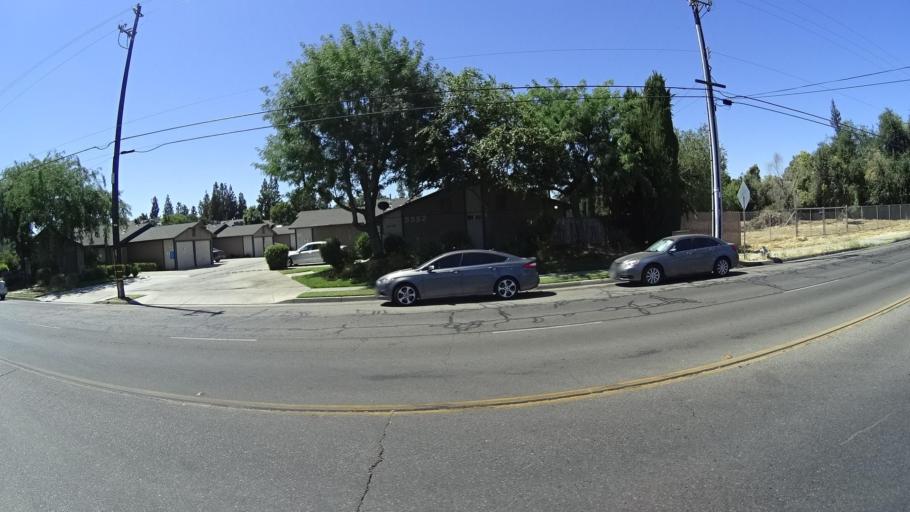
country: US
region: California
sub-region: Fresno County
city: Sunnyside
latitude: 36.7432
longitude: -119.7022
